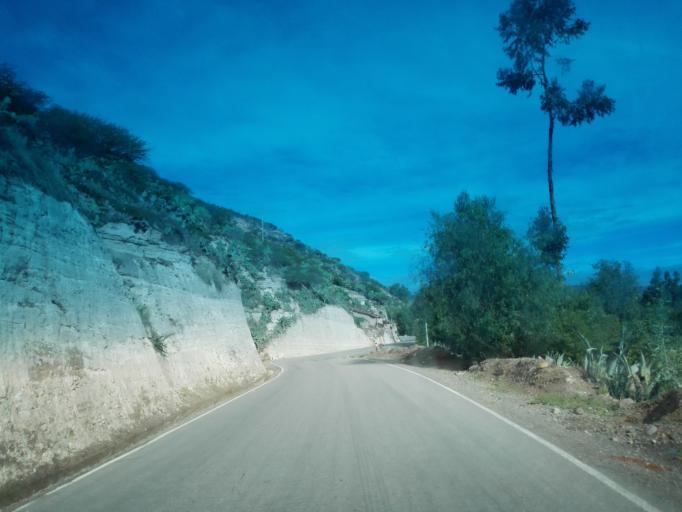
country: PE
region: Ayacucho
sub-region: Provincia de Huamanga
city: Pacaycasa
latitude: -13.0751
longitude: -74.2432
